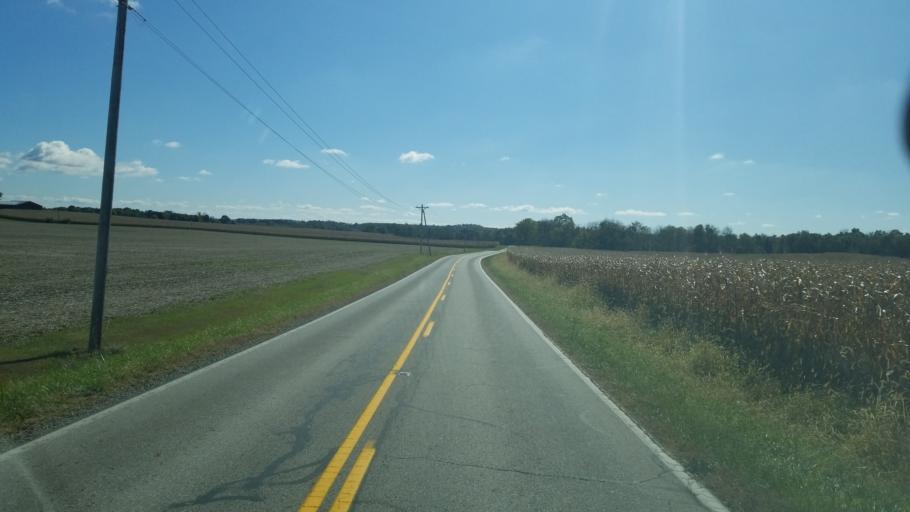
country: US
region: Ohio
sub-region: Highland County
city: Leesburg
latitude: 39.2828
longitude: -83.4979
